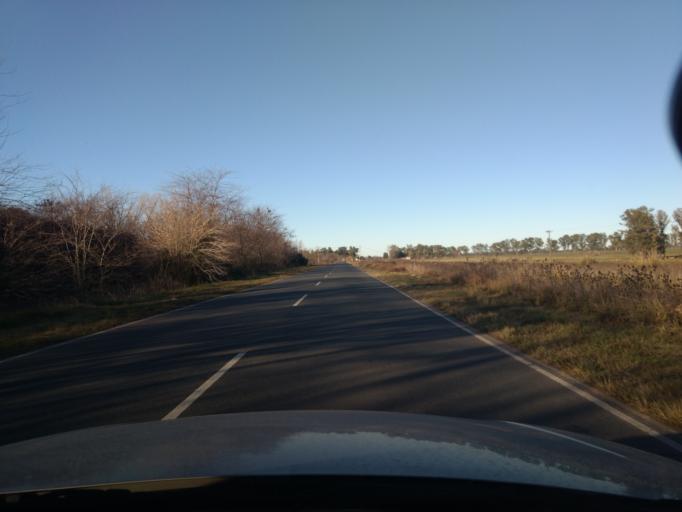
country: AR
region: Buenos Aires
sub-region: Partido de Lujan
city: Lujan
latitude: -34.6169
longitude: -59.1067
